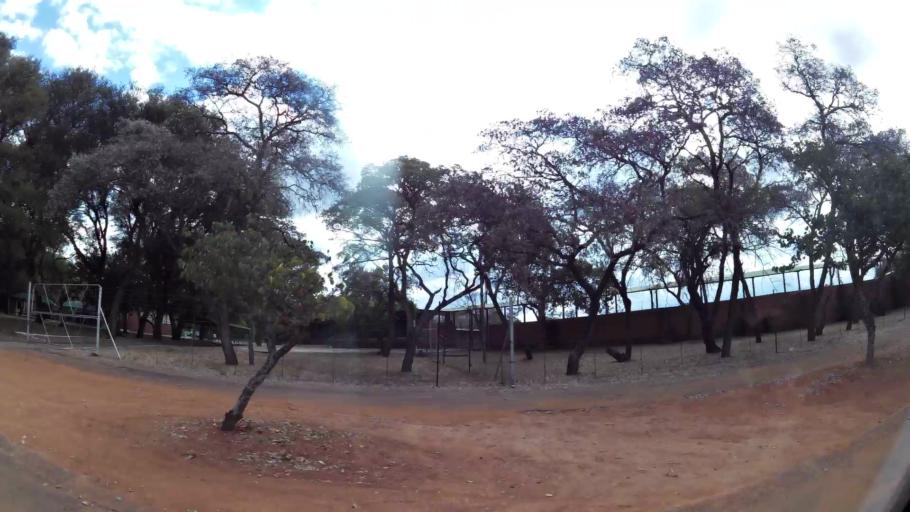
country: ZA
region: Limpopo
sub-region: Waterberg District Municipality
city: Modimolle
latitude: -24.7074
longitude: 28.3998
